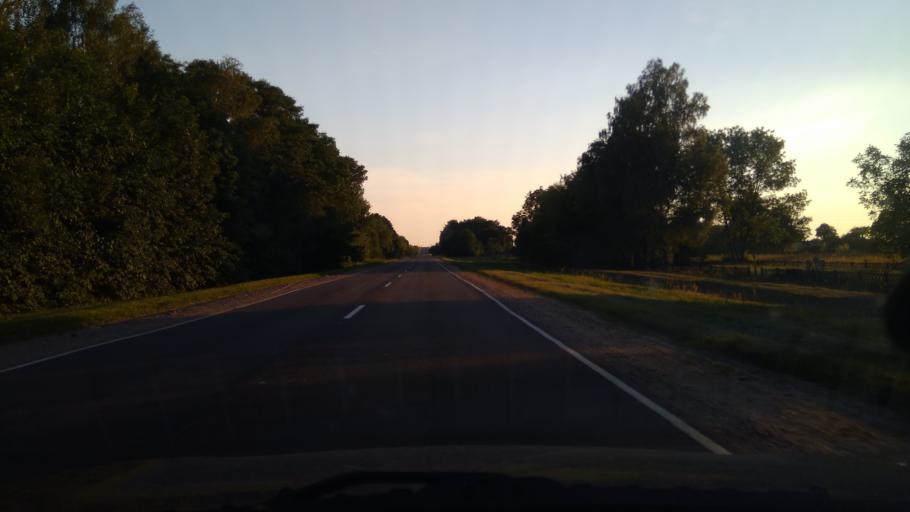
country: BY
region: Brest
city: Nyakhachava
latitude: 52.6444
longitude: 25.2063
